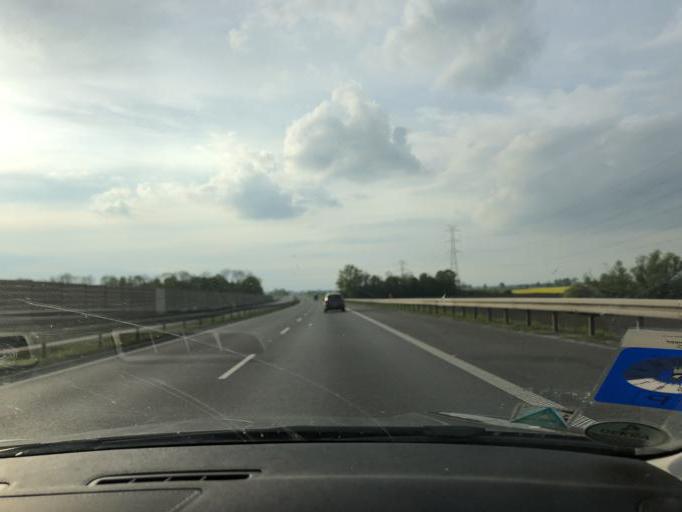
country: PL
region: Lower Silesian Voivodeship
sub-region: Powiat olawski
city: Wierzbno
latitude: 50.9356
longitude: 17.1112
